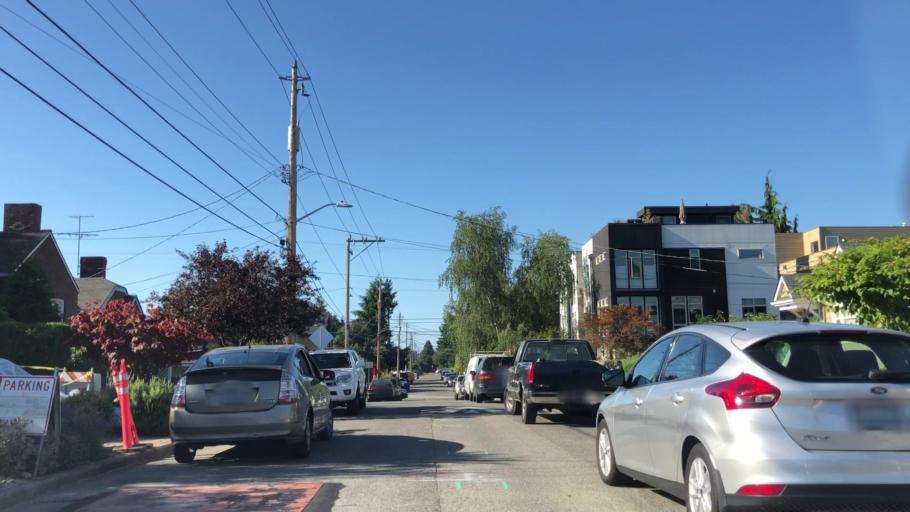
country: US
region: Washington
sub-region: King County
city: Shoreline
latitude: 47.6899
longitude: -122.3789
